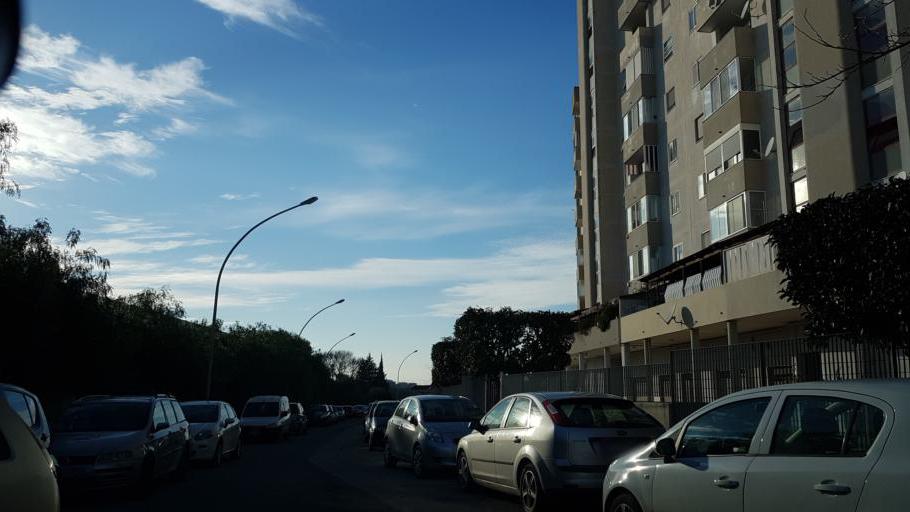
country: IT
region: Apulia
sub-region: Provincia di Brindisi
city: La Rosa
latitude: 40.6197
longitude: 17.9453
